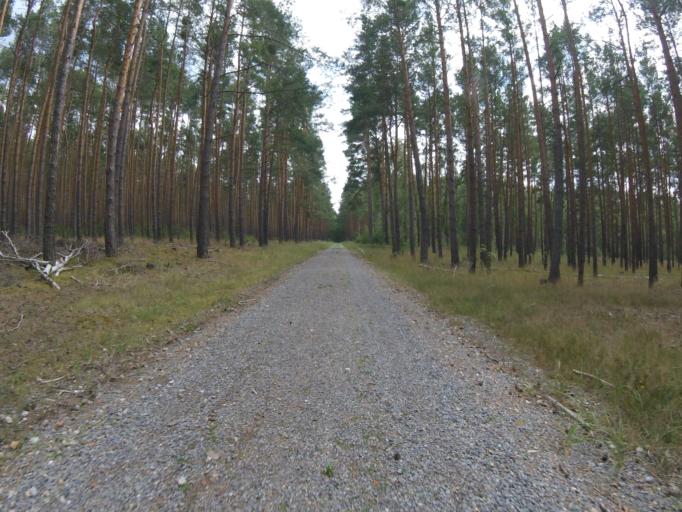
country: DE
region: Brandenburg
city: Gross Koris
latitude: 52.1546
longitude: 13.6722
